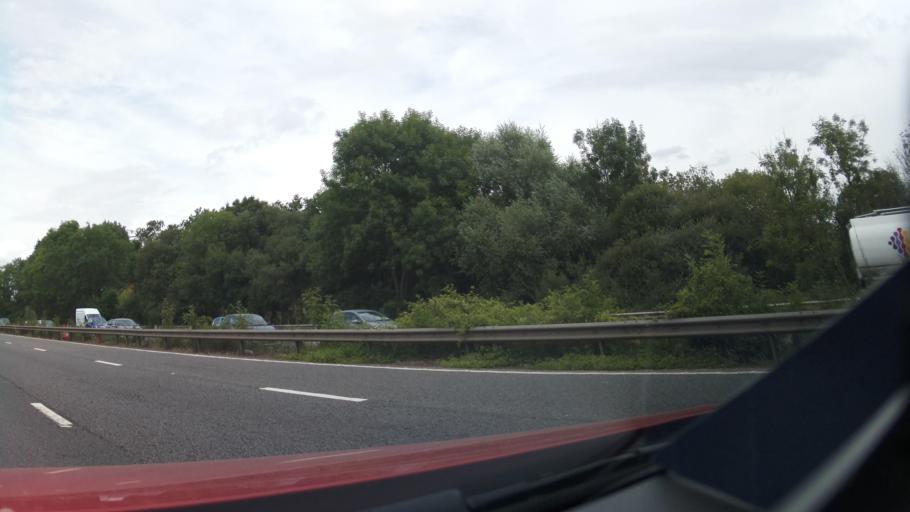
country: GB
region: England
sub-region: West Berkshire
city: Theale
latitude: 51.4539
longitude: -1.0816
